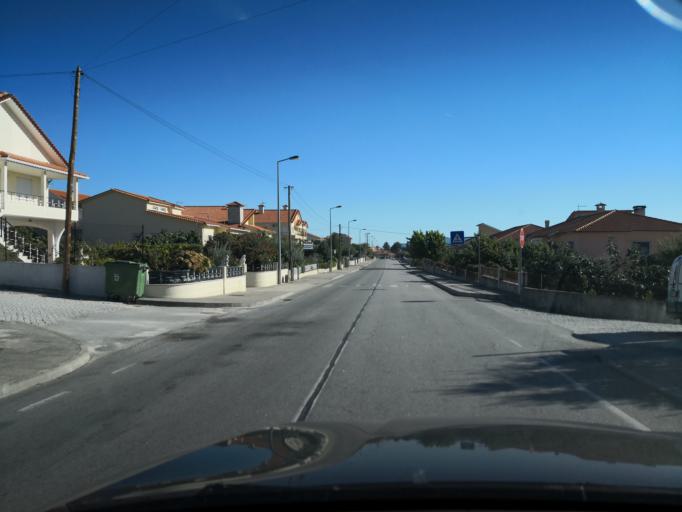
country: PT
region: Vila Real
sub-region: Valpacos
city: Valpacos
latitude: 41.6267
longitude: -7.3128
